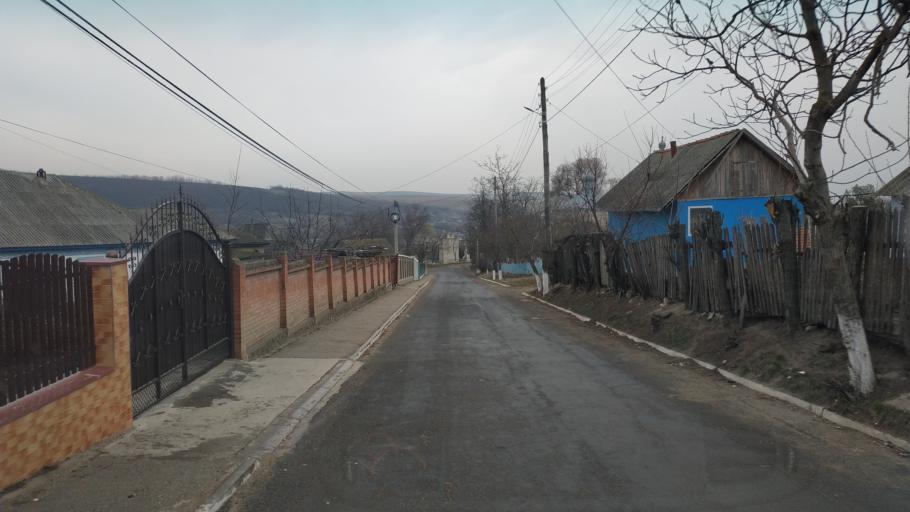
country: MD
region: Chisinau
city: Singera
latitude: 46.8293
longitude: 28.9736
